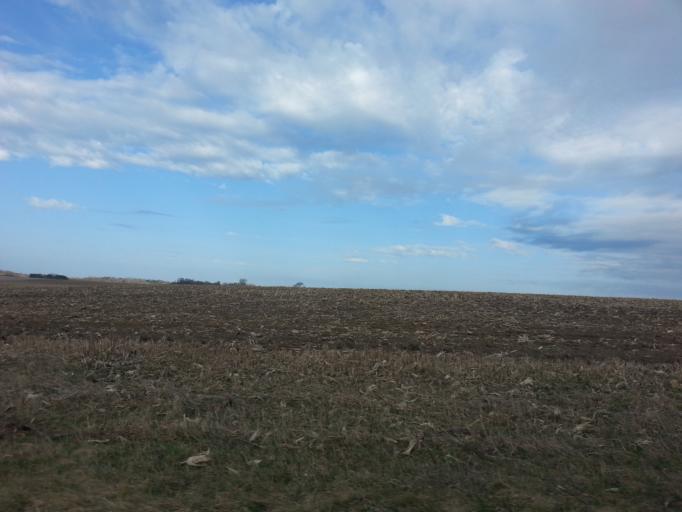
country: US
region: Minnesota
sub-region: Dakota County
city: Hastings
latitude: 44.8019
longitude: -92.8422
